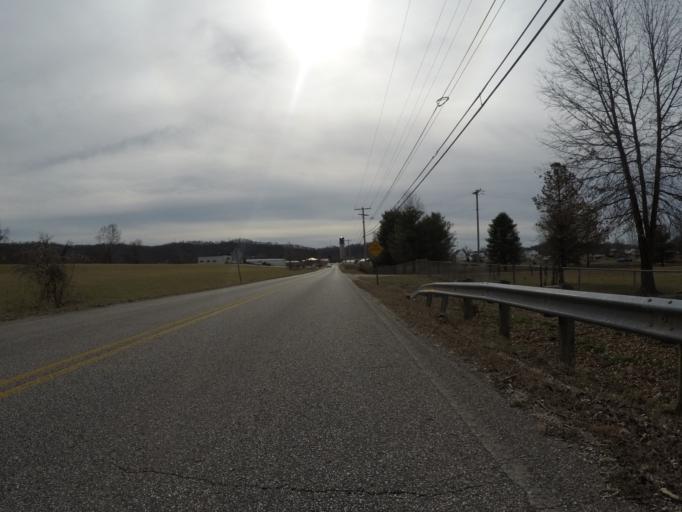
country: US
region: West Virginia
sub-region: Cabell County
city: Pea Ridge
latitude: 38.4425
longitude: -82.3765
